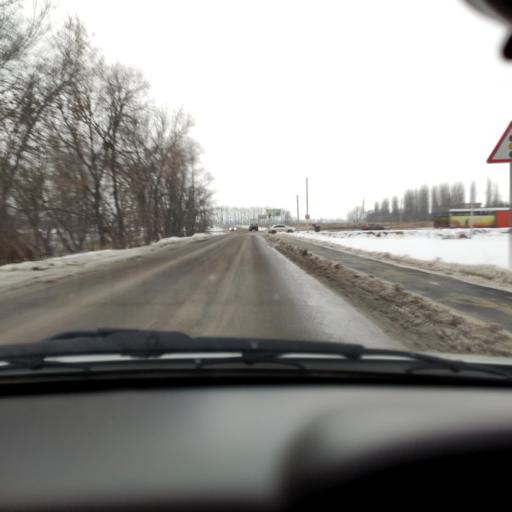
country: RU
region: Voronezj
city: Ramon'
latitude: 51.9182
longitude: 39.2914
